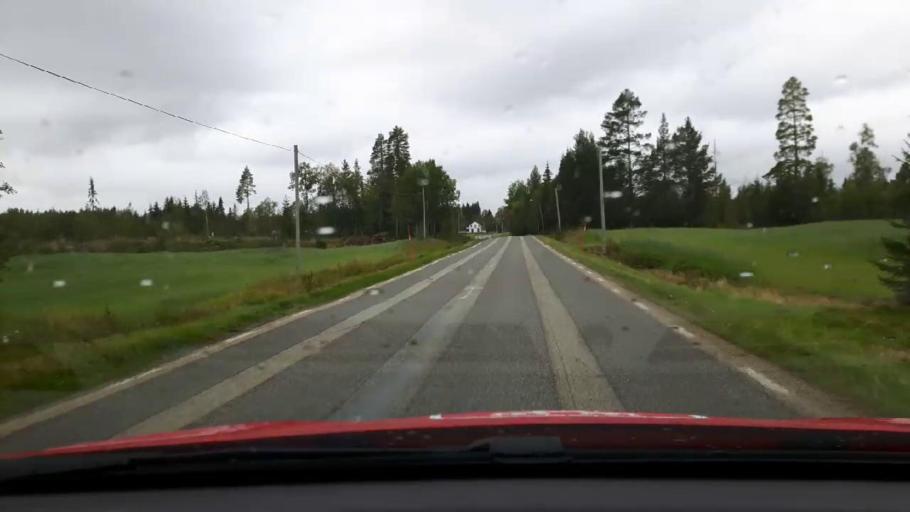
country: SE
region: Jaemtland
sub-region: Bergs Kommun
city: Hoverberg
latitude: 62.8147
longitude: 14.4118
